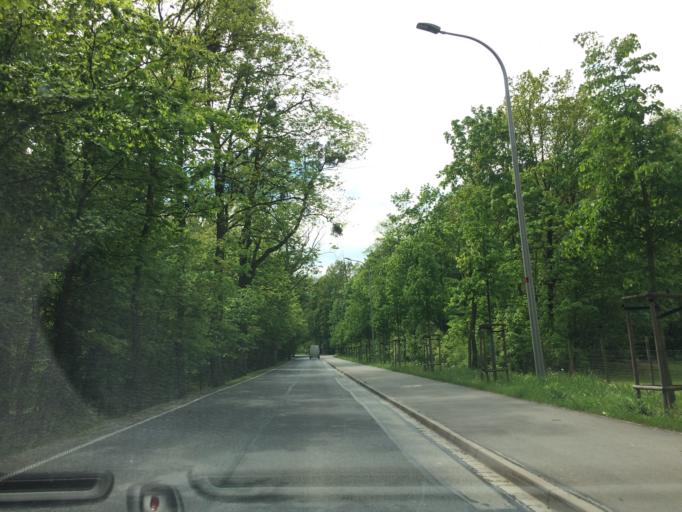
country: PL
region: Lower Silesian Voivodeship
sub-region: Powiat wroclawski
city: Smolec
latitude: 51.1563
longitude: 16.8746
